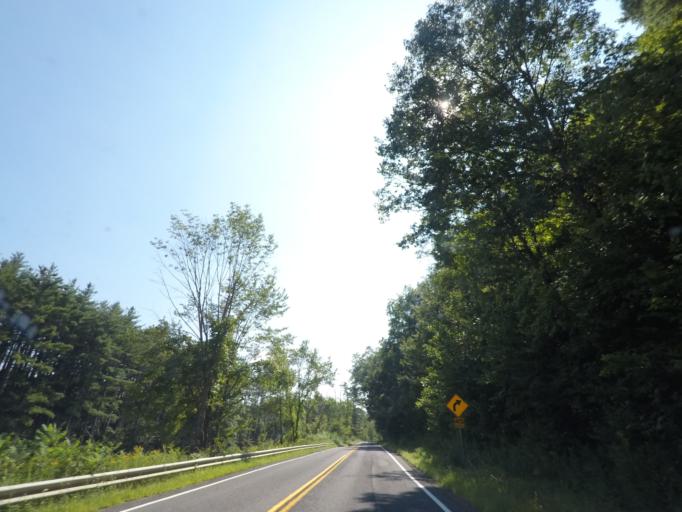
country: US
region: New York
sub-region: Rensselaer County
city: Hoosick Falls
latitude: 42.8297
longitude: -73.4770
